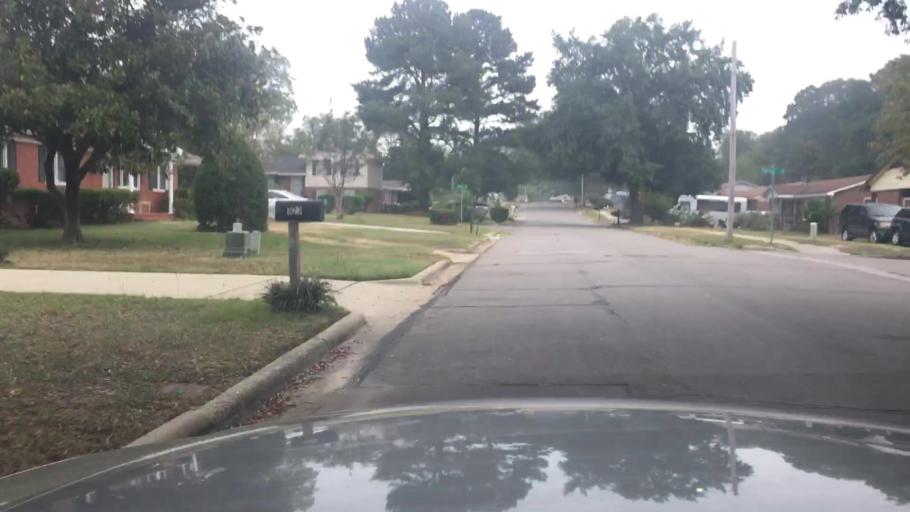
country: US
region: North Carolina
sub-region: Cumberland County
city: Fayetteville
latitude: 35.0684
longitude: -78.8860
